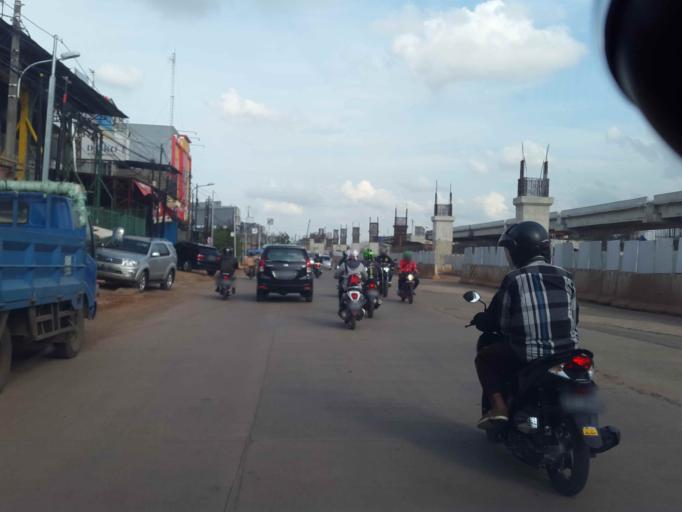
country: ID
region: West Java
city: Bekasi
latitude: -6.2491
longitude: 106.9381
